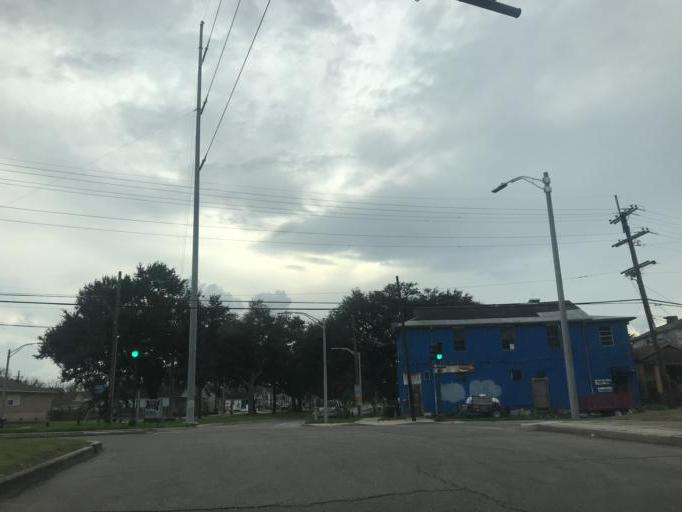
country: US
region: Louisiana
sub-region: Orleans Parish
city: New Orleans
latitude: 29.9491
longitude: -90.0932
